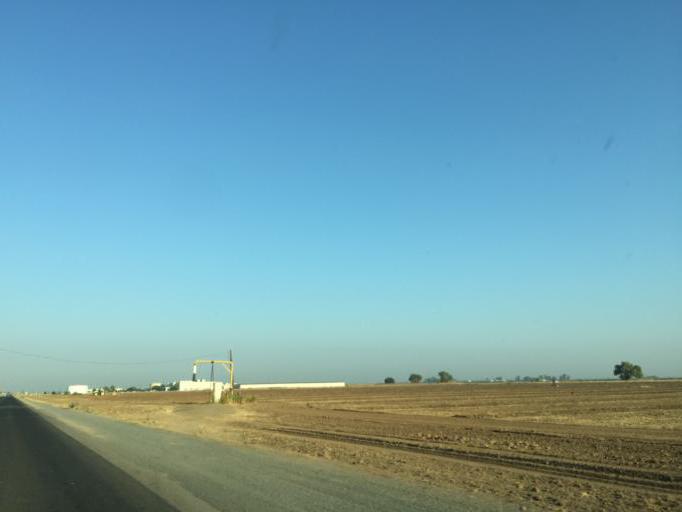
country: US
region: California
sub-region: Tulare County
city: Cutler
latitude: 36.4580
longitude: -119.3142
